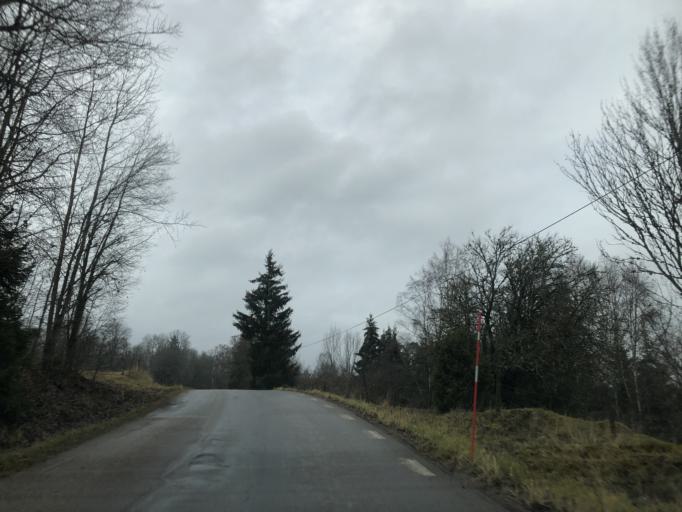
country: SE
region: Vaestra Goetaland
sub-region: Ulricehamns Kommun
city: Ulricehamn
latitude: 57.8788
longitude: 13.5208
